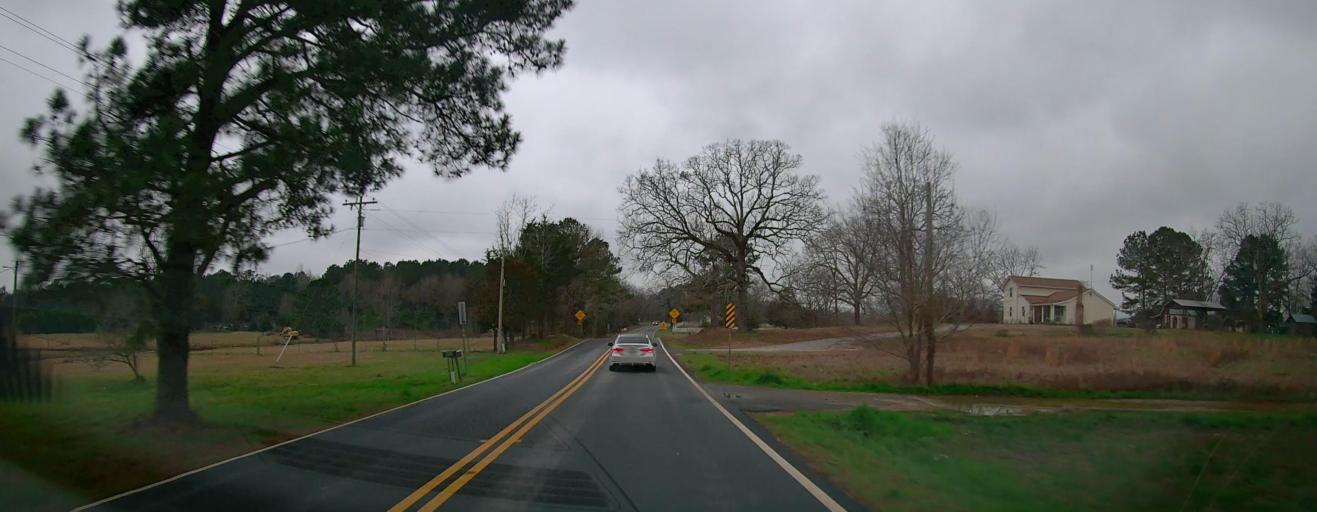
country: US
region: Georgia
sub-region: Pike County
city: Zebulon
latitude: 33.0588
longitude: -84.2613
